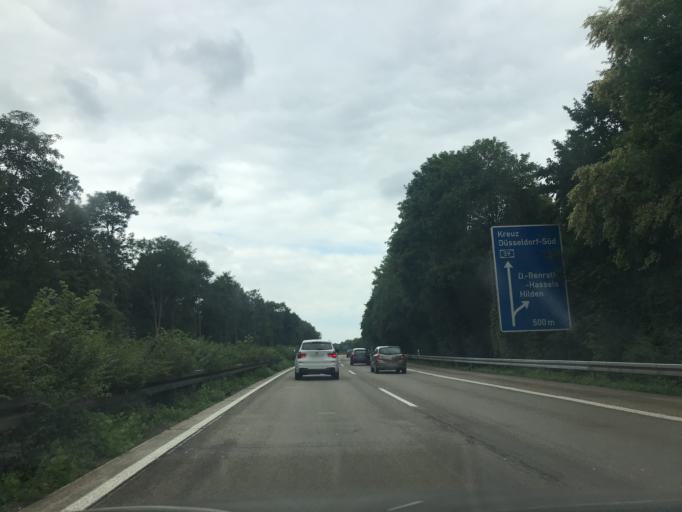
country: DE
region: North Rhine-Westphalia
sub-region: Regierungsbezirk Dusseldorf
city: Hilden
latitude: 51.1706
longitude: 6.8851
